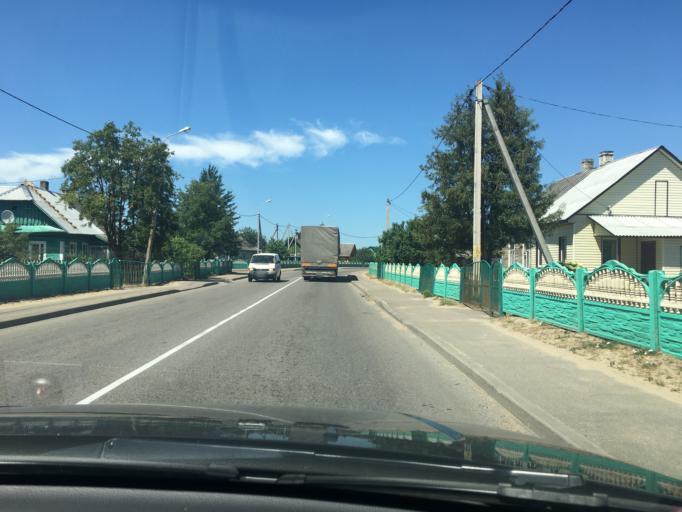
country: BY
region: Grodnenskaya
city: Iwye
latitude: 54.0338
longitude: 25.9239
